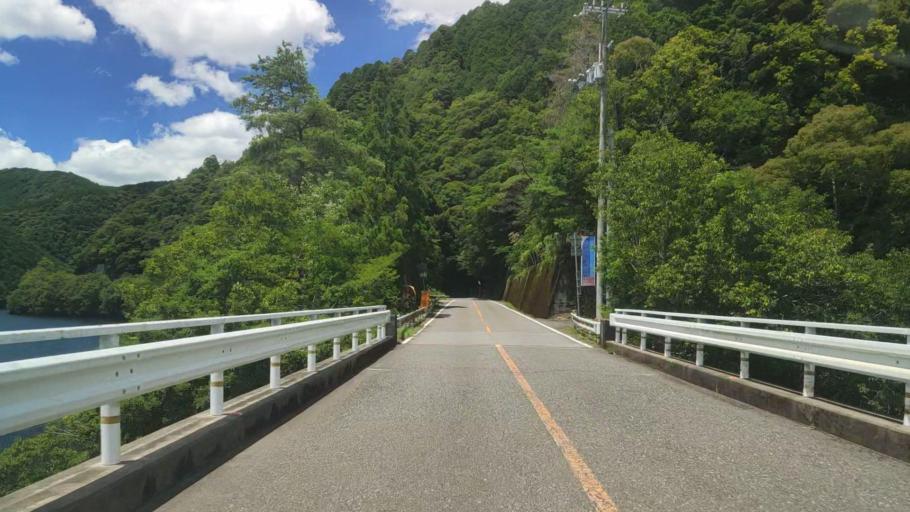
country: JP
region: Mie
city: Owase
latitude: 33.9977
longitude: 136.0224
